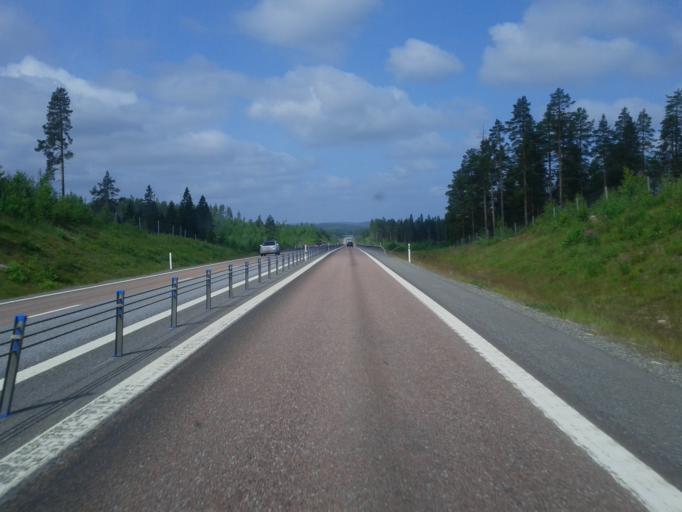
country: SE
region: Vaesterbotten
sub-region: Skelleftea Kommun
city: Soedra Bergsbyn
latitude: 64.6880
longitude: 21.0504
